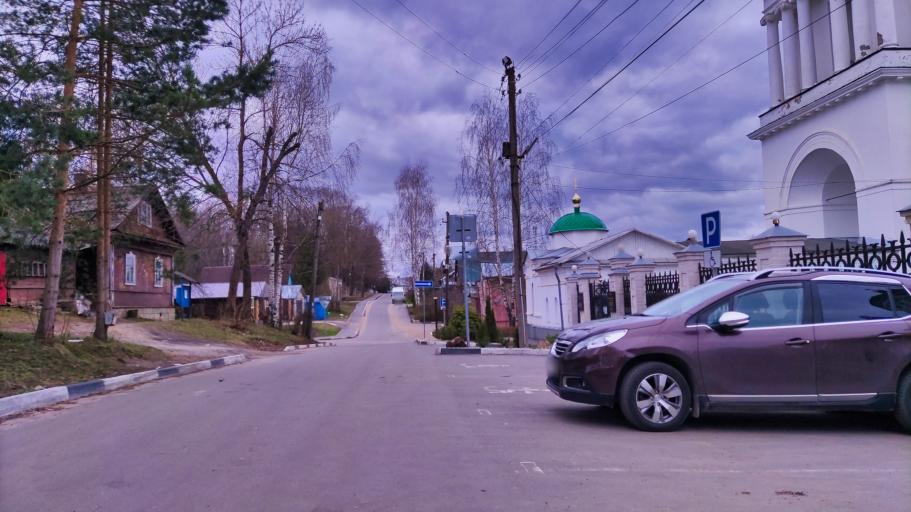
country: RU
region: Tverskaya
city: Rzhev
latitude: 56.2548
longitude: 34.3365
